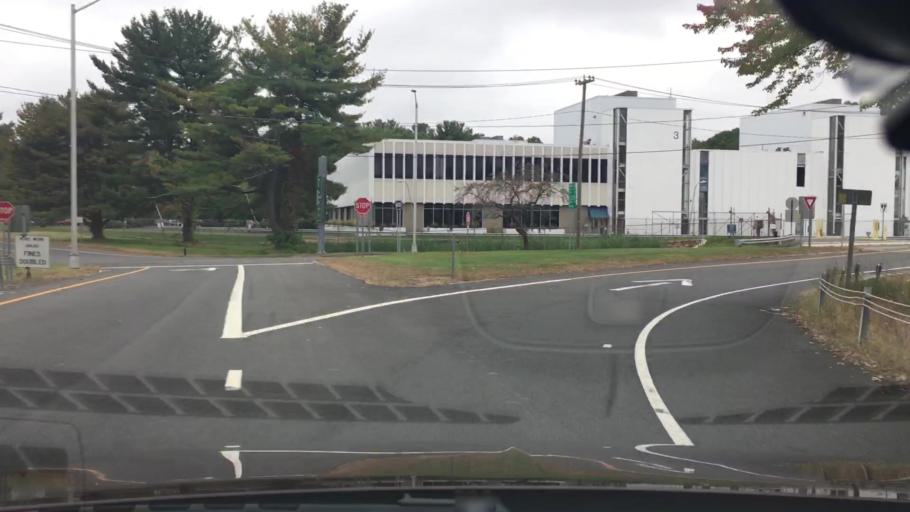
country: US
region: Connecticut
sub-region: Hartford County
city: Windsor Locks
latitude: 41.9186
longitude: -72.6842
